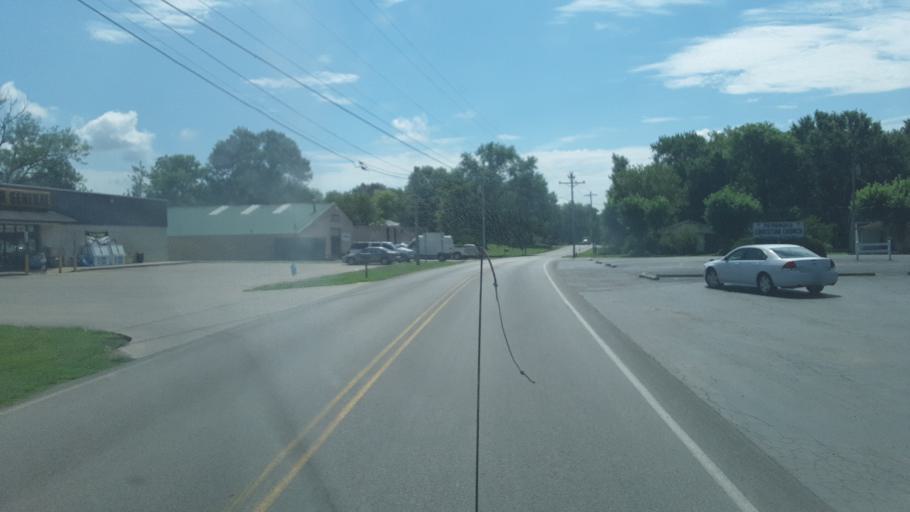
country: US
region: Kentucky
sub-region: Christian County
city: Oak Grove
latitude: 36.7784
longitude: -87.3537
